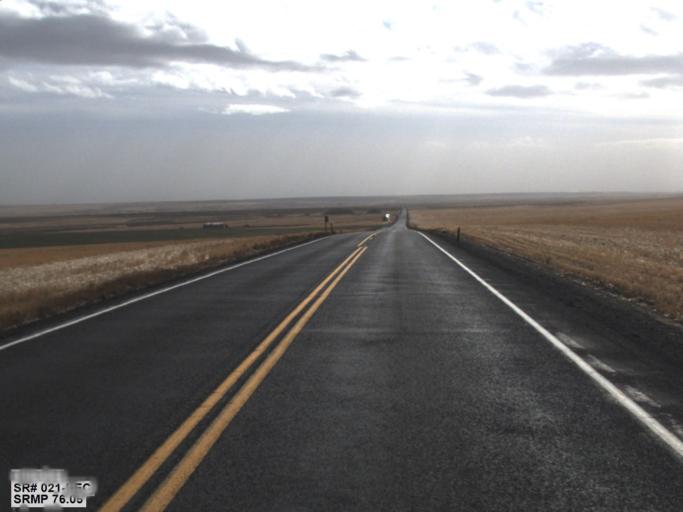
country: US
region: Washington
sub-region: Okanogan County
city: Coulee Dam
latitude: 47.5824
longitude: -118.7860
